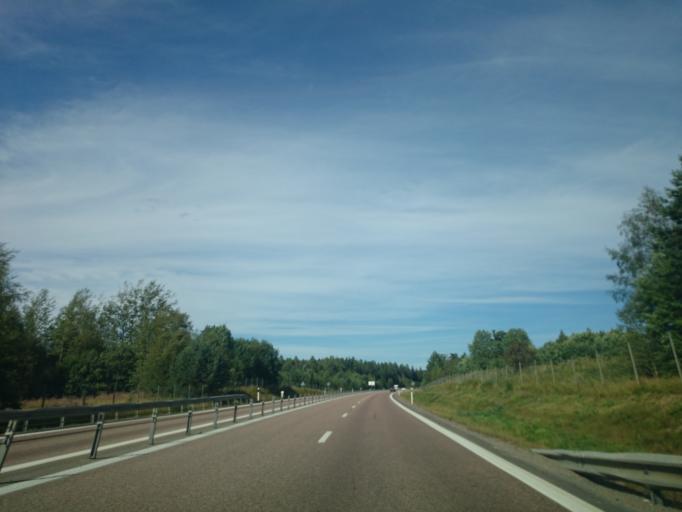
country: SE
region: Gaevleborg
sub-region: Hudiksvalls Kommun
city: Hudiksvall
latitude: 61.7659
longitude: 17.0959
